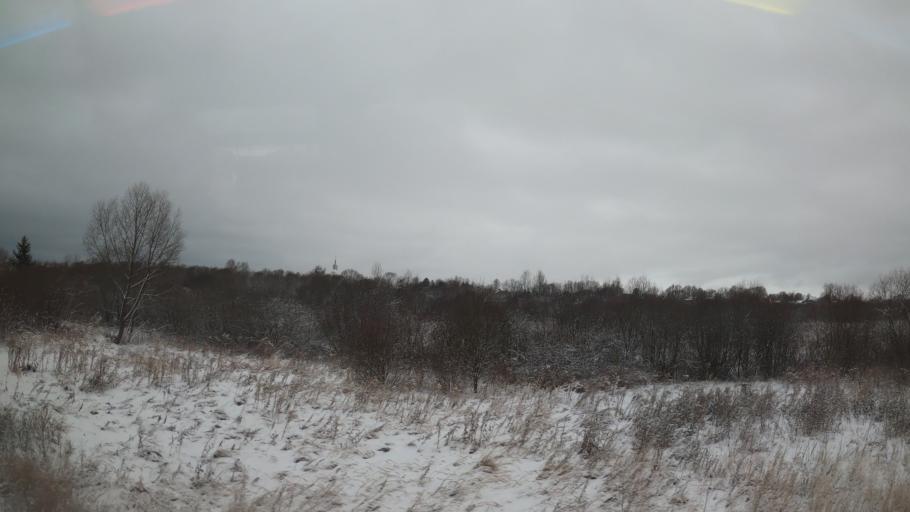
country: RU
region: Jaroslavl
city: Pereslavl'-Zalesskiy
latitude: 56.7053
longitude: 38.9095
